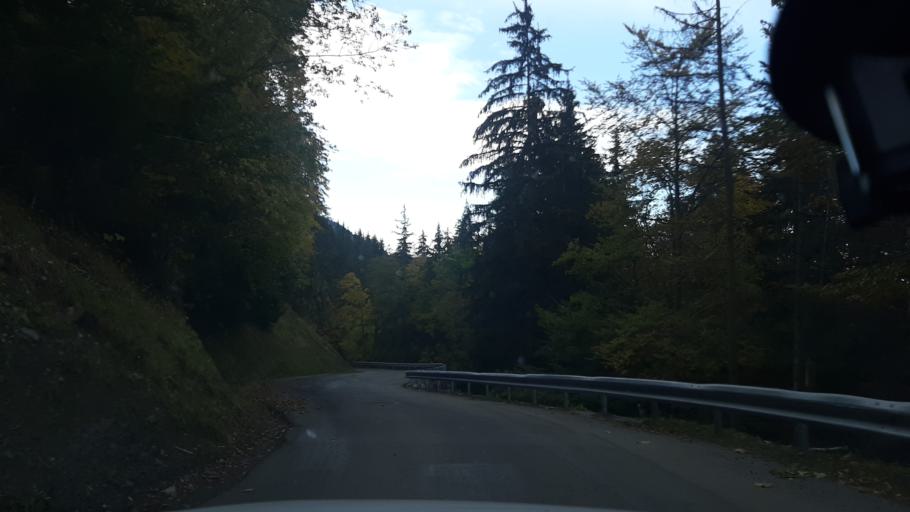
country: FR
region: Rhone-Alpes
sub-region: Departement de la Savoie
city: Villargondran
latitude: 45.1994
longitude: 6.3210
